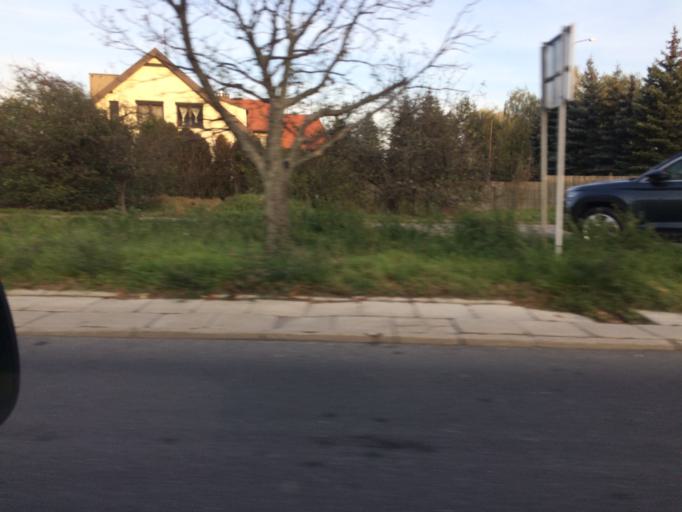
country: PL
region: Opole Voivodeship
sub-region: Powiat opolski
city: Opole
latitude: 50.6741
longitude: 17.9752
